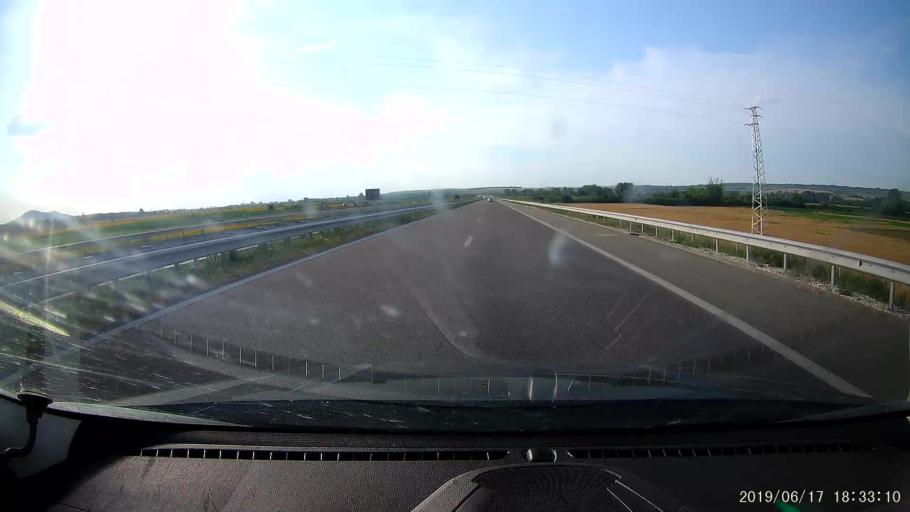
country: BG
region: Khaskovo
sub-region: Obshtina Dimitrovgrad
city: Dimitrovgrad
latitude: 42.0738
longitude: 25.4640
